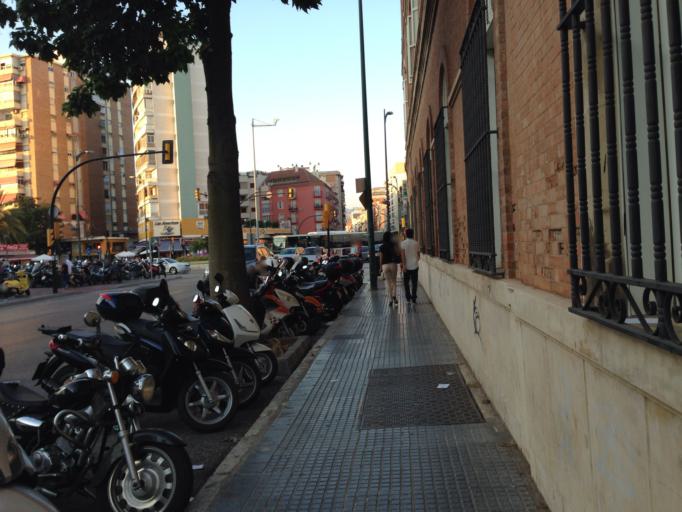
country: ES
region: Andalusia
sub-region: Provincia de Malaga
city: Malaga
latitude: 36.7114
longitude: -4.4309
